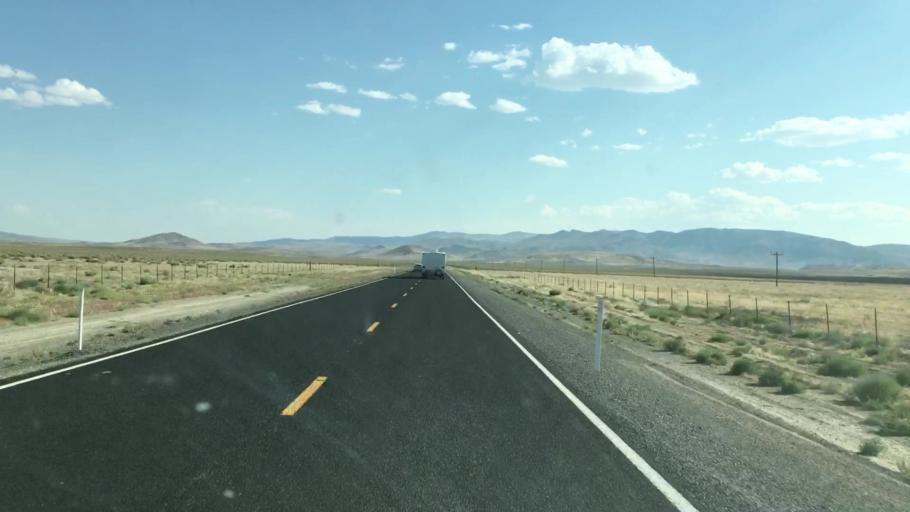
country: US
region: Nevada
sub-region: Lyon County
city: Fernley
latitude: 39.6788
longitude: -119.3338
